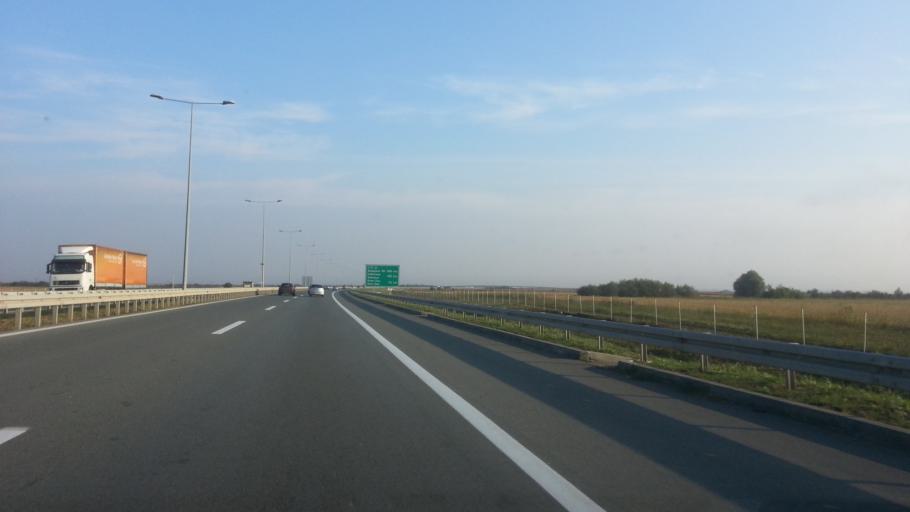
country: RS
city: Dobanovci
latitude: 44.8479
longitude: 20.2495
